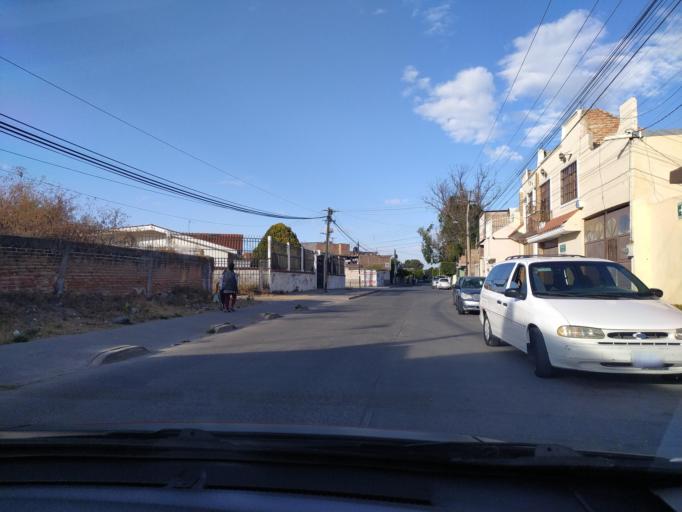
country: MX
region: Guanajuato
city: San Francisco del Rincon
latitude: 21.0115
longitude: -101.8670
